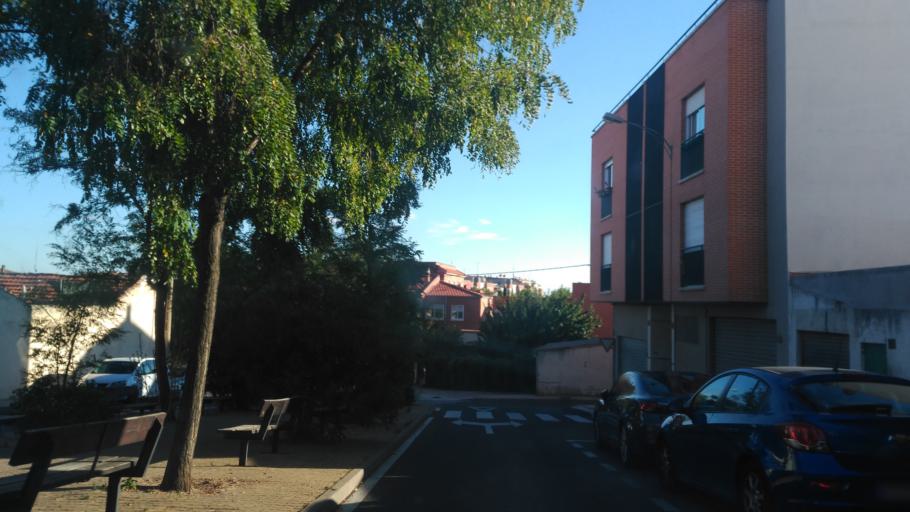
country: ES
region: Castille and Leon
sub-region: Provincia de Salamanca
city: Salamanca
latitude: 40.9765
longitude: -5.6707
